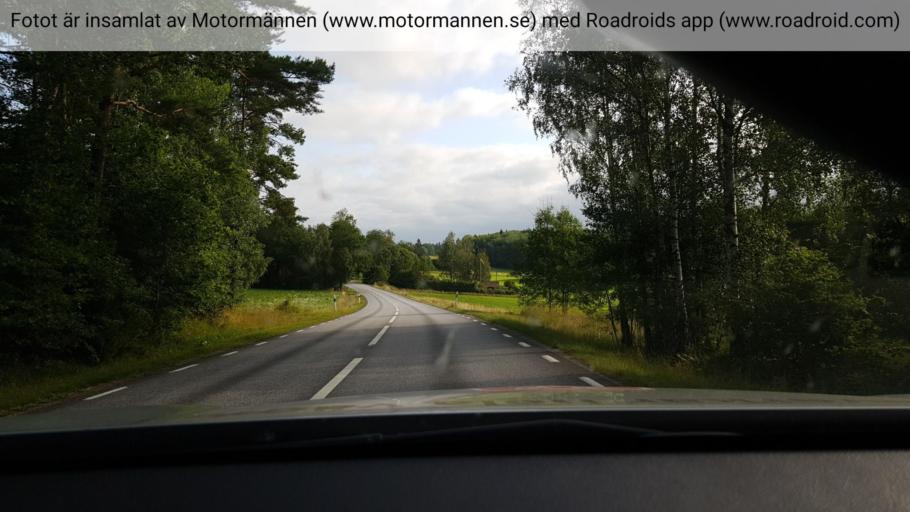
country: SE
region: Stockholm
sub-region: Norrtalje Kommun
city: Rimbo
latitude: 59.6783
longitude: 18.3622
